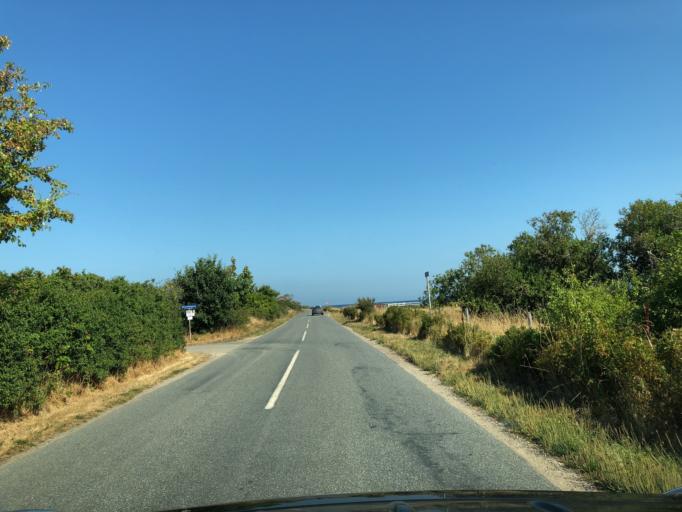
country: DK
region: Zealand
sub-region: Odsherred Kommune
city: Asnaes
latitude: 55.9988
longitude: 11.2882
